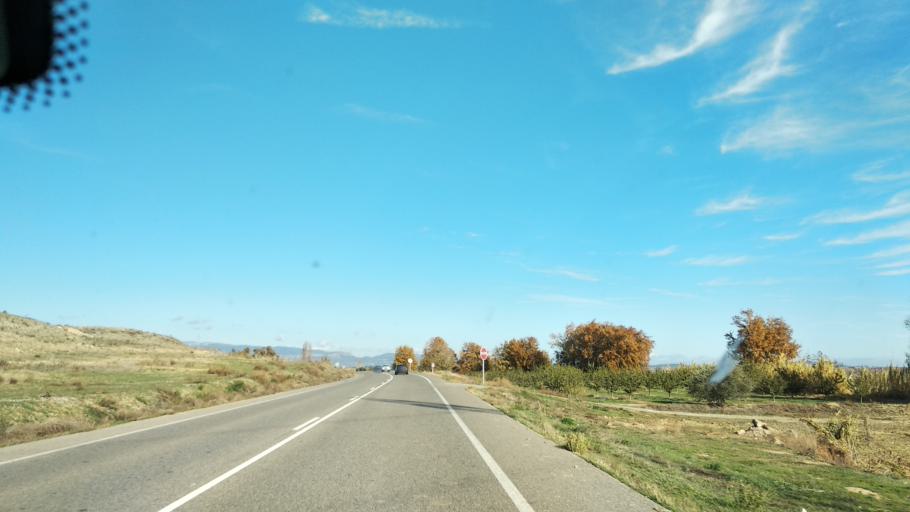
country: ES
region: Catalonia
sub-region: Provincia de Lleida
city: Termens
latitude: 41.7438
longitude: 0.7600
